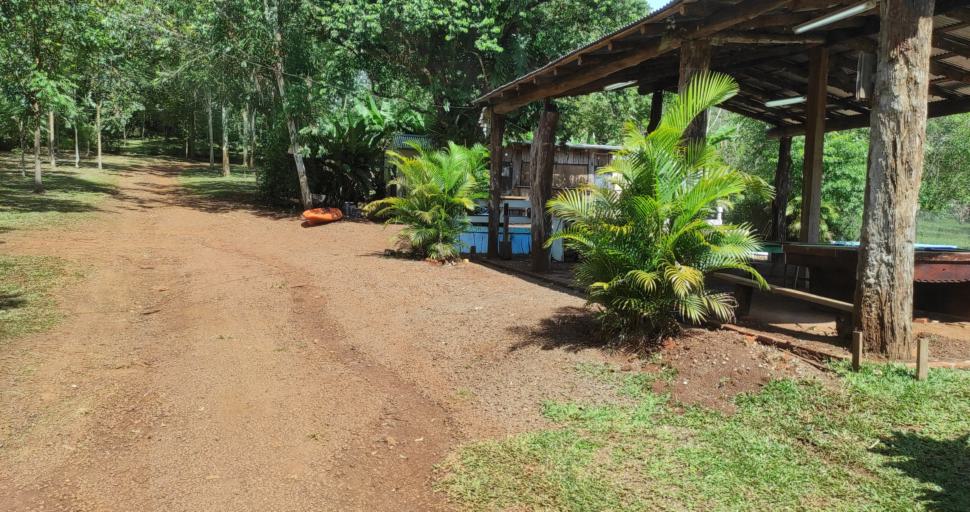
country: AR
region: Misiones
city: El Soberbio
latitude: -27.2851
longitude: -54.1960
